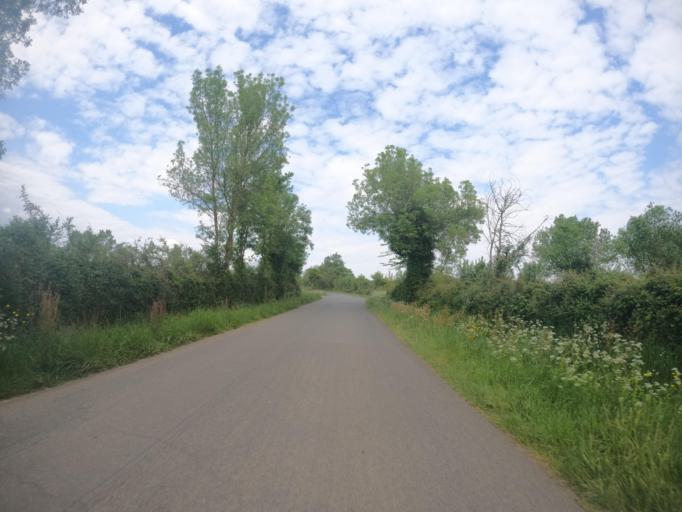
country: FR
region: Poitou-Charentes
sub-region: Departement des Deux-Sevres
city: Saint-Varent
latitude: 46.8791
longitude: -0.2950
